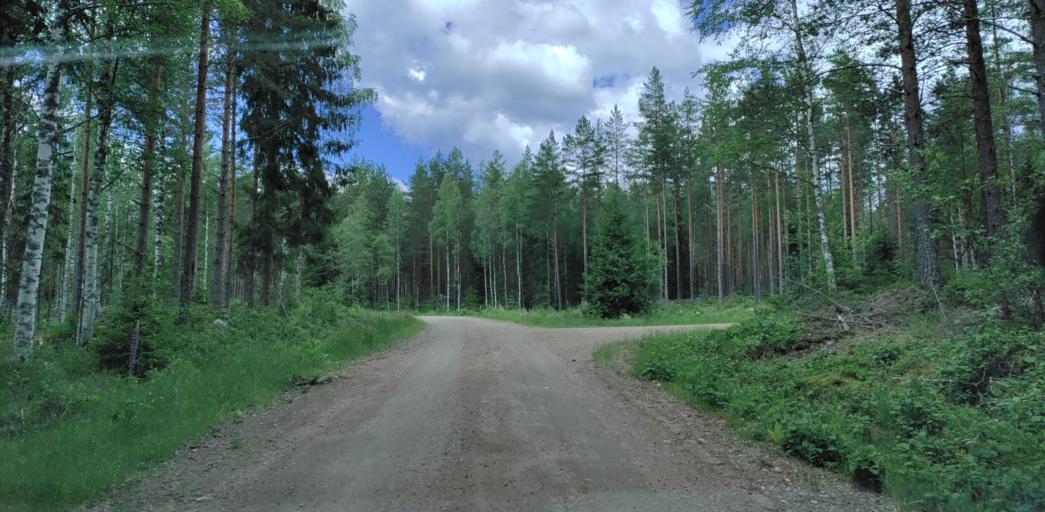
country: SE
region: Vaermland
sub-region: Hagfors Kommun
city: Ekshaerad
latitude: 60.0927
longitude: 13.4081
